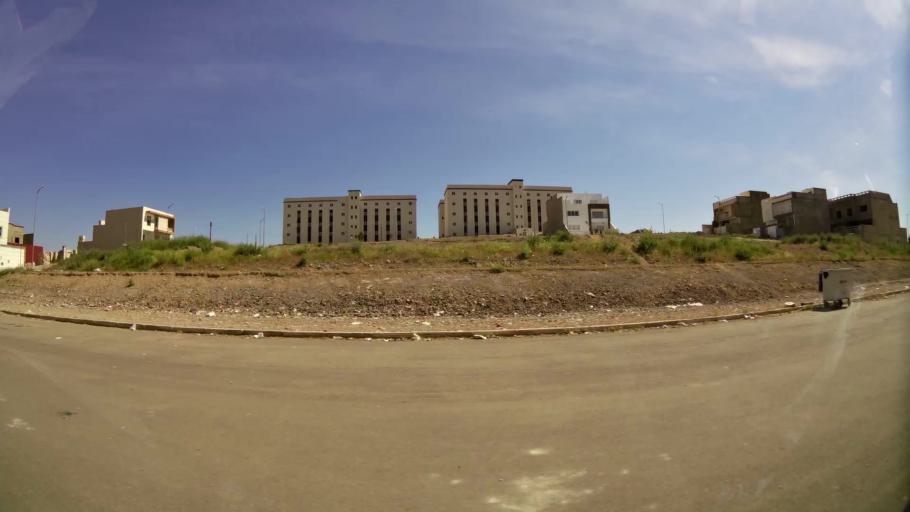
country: MA
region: Oriental
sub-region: Oujda-Angad
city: Oujda
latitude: 34.6532
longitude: -1.9100
